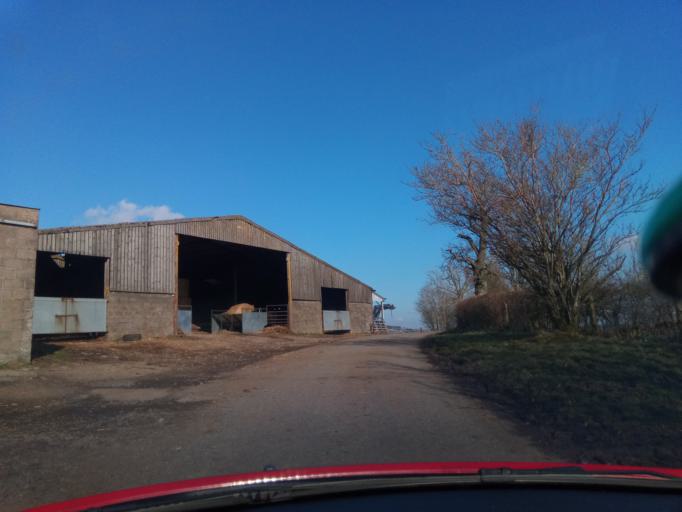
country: GB
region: Scotland
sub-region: The Scottish Borders
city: Hawick
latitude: 55.4992
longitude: -2.7732
